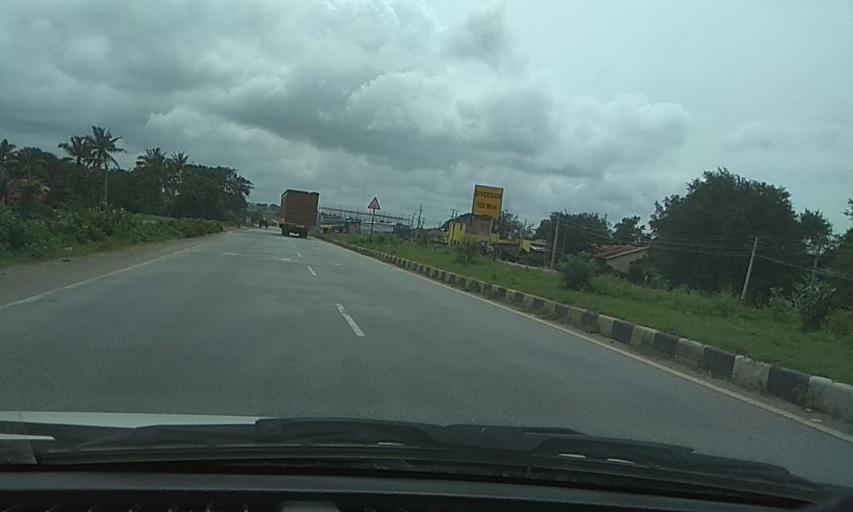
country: IN
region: Karnataka
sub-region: Davanagere
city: Mayakonda
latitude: 14.3664
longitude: 76.1565
